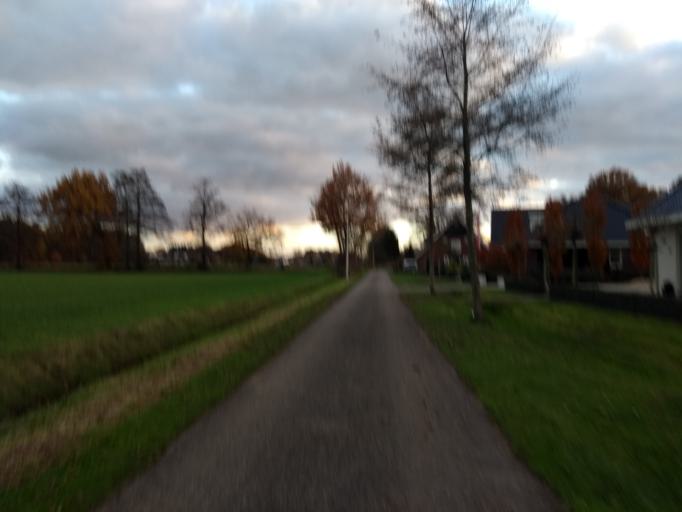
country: NL
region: Overijssel
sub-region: Gemeente Almelo
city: Almelo
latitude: 52.3842
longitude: 6.7018
